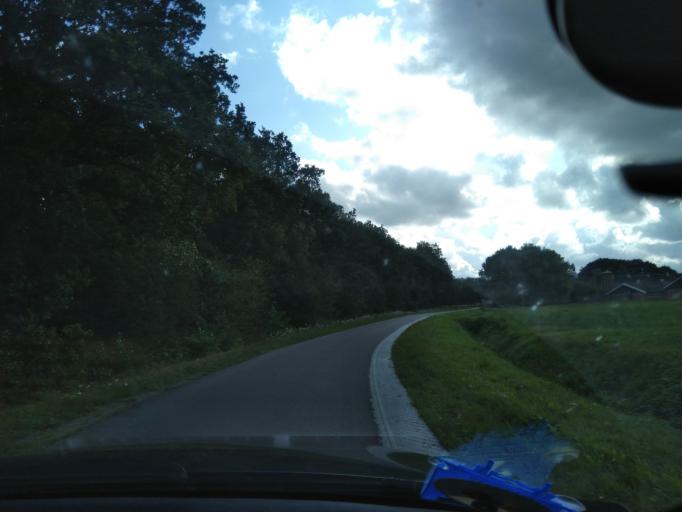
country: NL
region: Drenthe
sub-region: Gemeente Tynaarlo
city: Vries
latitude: 53.0750
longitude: 6.5476
